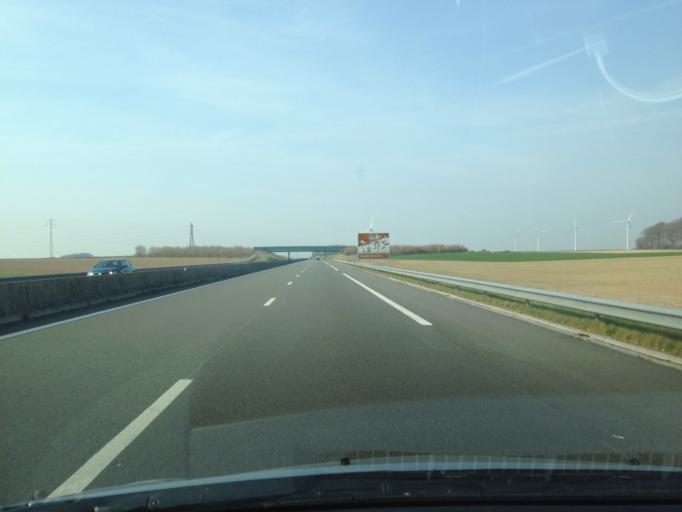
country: FR
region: Picardie
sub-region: Departement de la Somme
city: Rue
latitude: 50.2832
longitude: 1.7327
